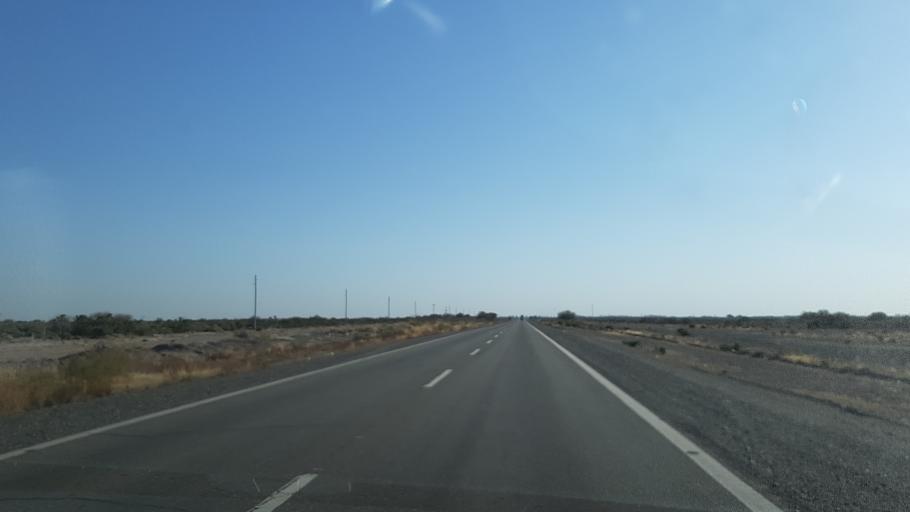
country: AR
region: San Juan
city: Villa Media Agua
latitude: -32.1506
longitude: -68.4822
